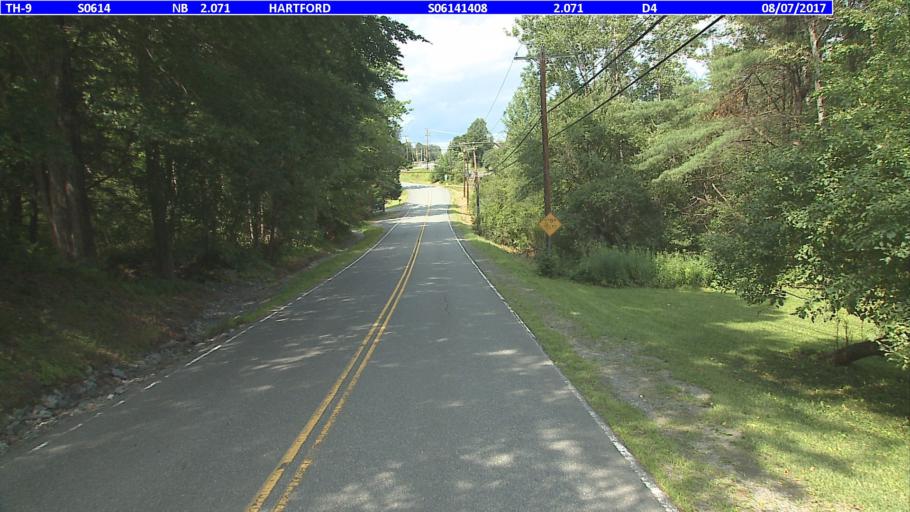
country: US
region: Vermont
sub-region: Windsor County
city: Wilder
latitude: 43.6837
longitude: -72.3216
